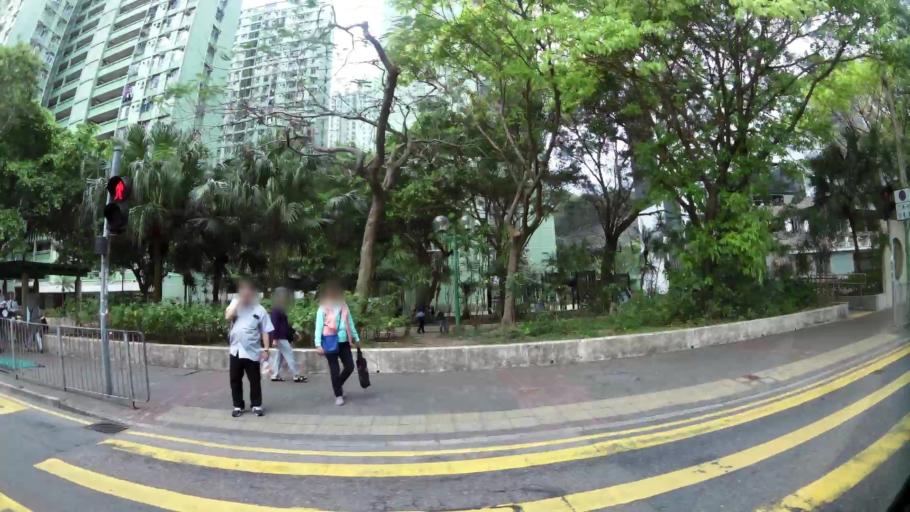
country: HK
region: Wanchai
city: Wan Chai
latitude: 22.2642
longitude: 114.2484
